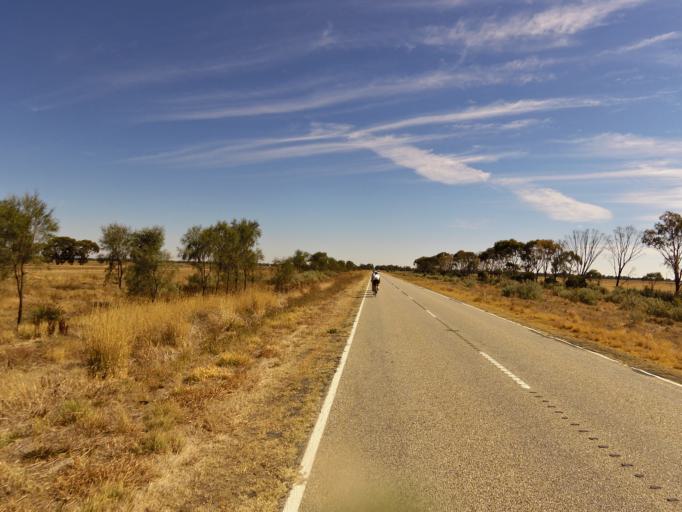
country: AU
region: Victoria
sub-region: Greater Bendigo
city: Long Gully
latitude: -36.1369
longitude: 143.8118
